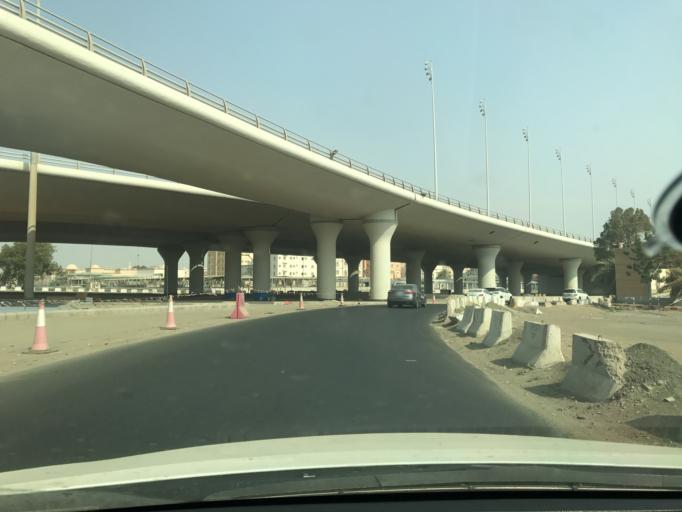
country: SA
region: Makkah
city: Jeddah
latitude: 21.6311
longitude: 39.1814
